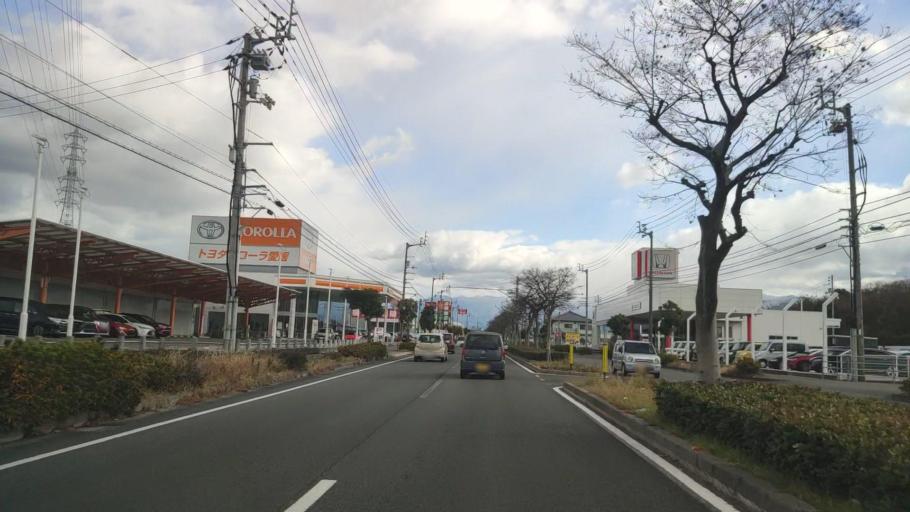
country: JP
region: Ehime
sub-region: Shikoku-chuo Shi
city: Matsuyama
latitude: 33.8203
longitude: 132.7889
